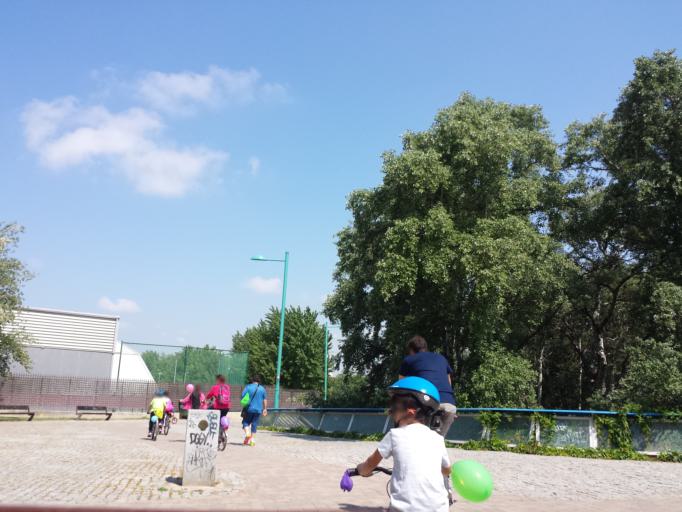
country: ES
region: Aragon
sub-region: Provincia de Zaragoza
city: Almozara
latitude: 41.6639
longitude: -0.8958
